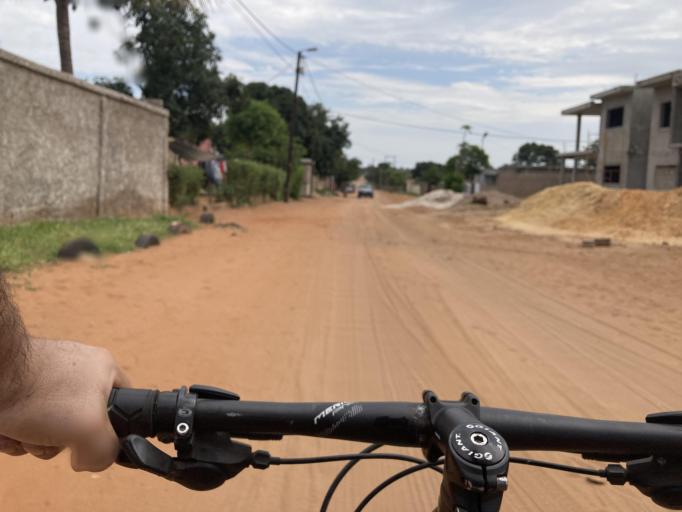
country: MZ
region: Maputo City
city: Maputo
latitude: -25.8899
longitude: 32.6088
